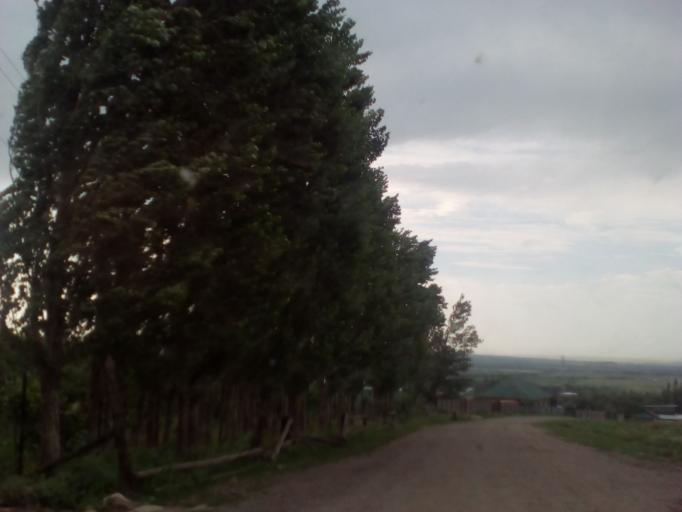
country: KZ
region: Almaty Oblysy
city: Burunday
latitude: 43.1502
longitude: 76.3856
